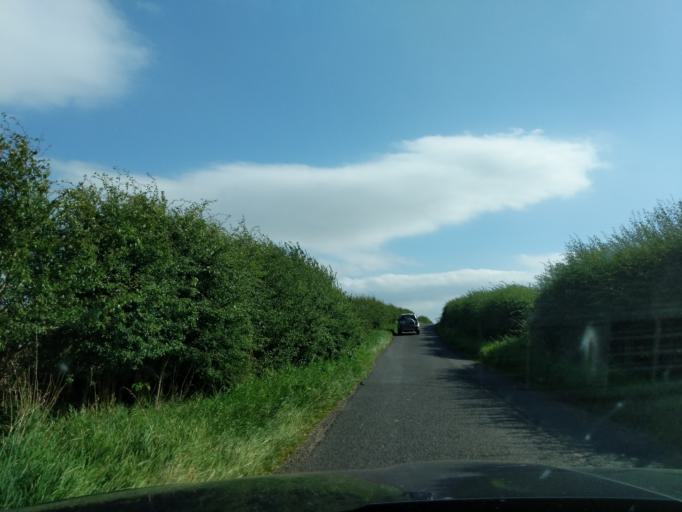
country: GB
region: England
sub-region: Northumberland
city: Ford
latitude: 55.6640
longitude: -2.1601
